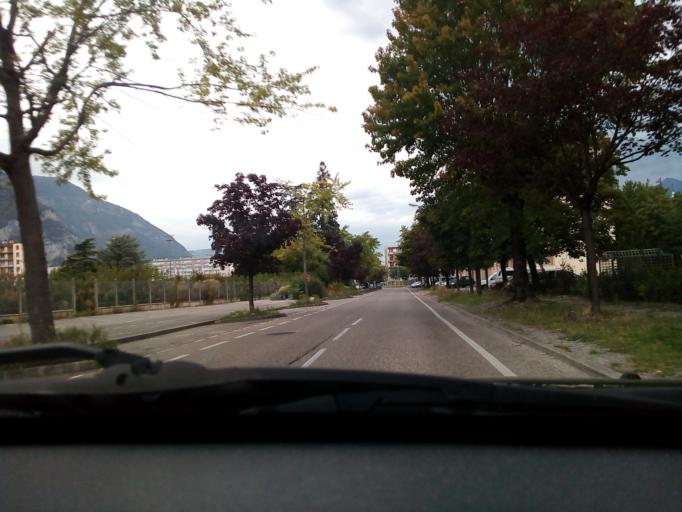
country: FR
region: Rhone-Alpes
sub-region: Departement de l'Isere
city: Seyssinet-Pariset
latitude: 45.1864
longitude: 5.6908
